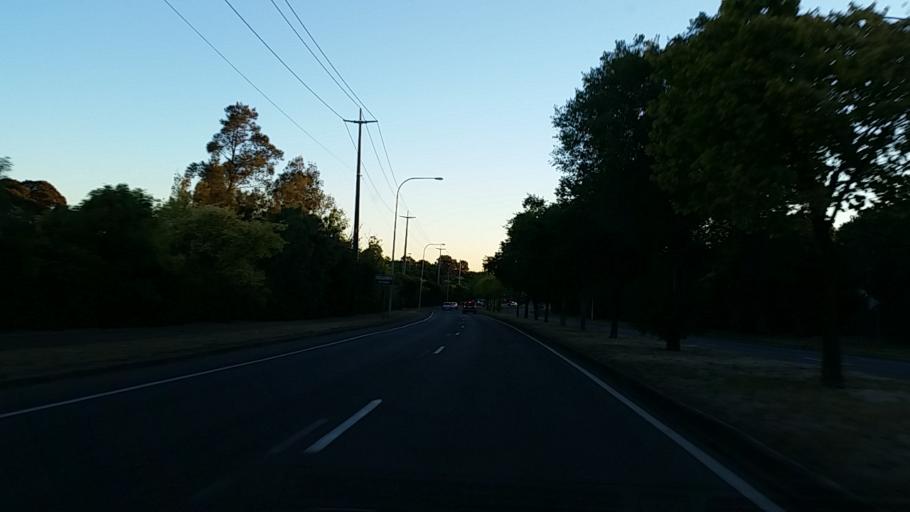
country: AU
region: South Australia
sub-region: Tea Tree Gully
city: Modbury
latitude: -34.8012
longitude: 138.6851
